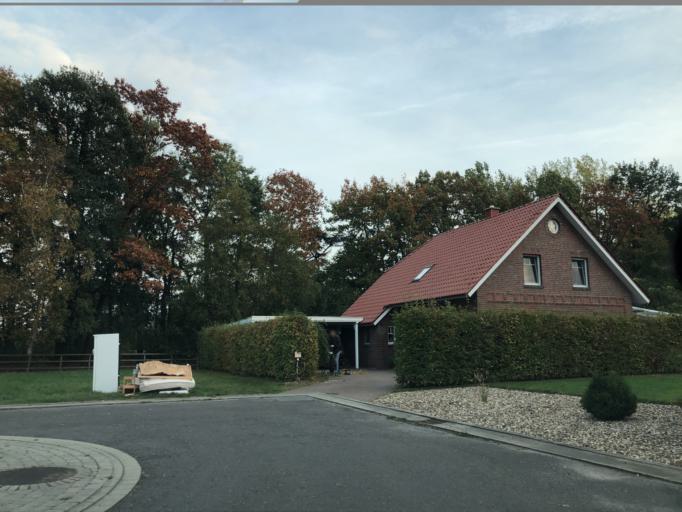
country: DE
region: Lower Saxony
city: Papenburg
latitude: 53.0418
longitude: 7.3953
